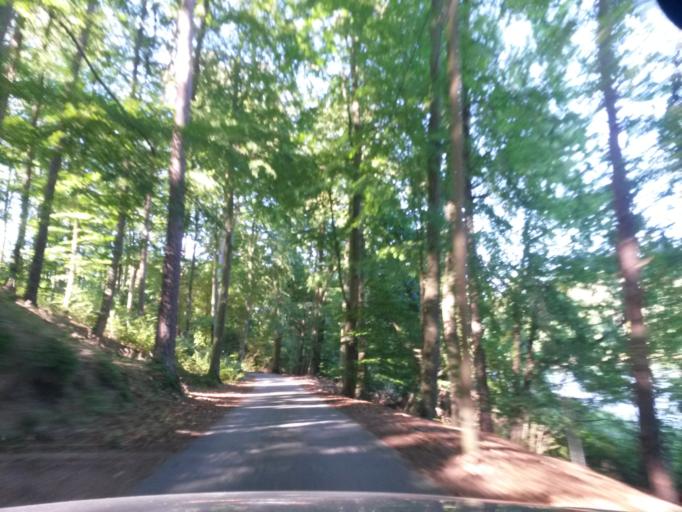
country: DE
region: Brandenburg
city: Lychen
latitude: 53.1817
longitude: 13.3518
